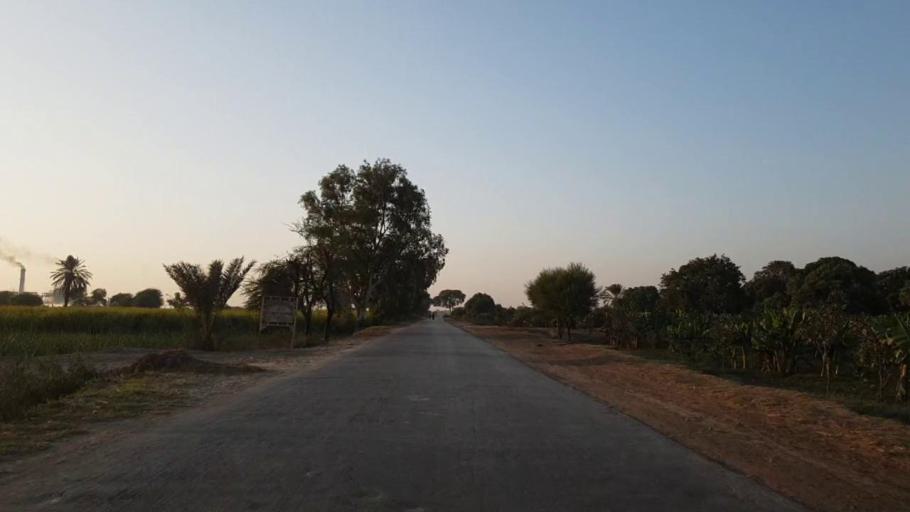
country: PK
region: Sindh
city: Chambar
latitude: 25.2489
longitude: 68.6791
